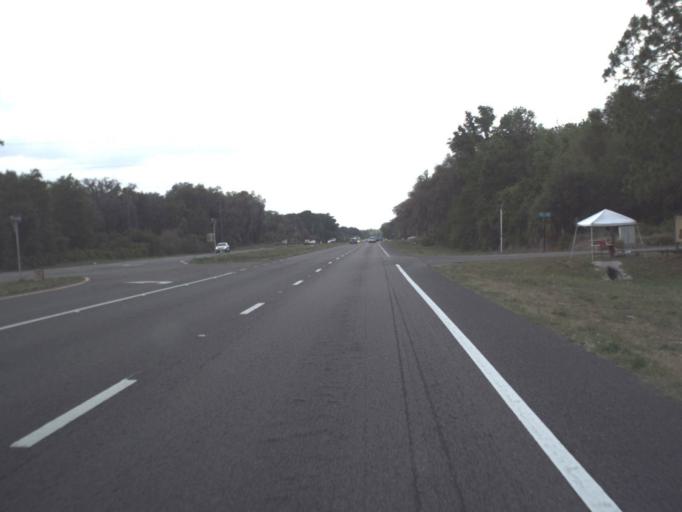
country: US
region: Florida
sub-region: Citrus County
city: Inverness
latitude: 28.8540
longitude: -82.2072
